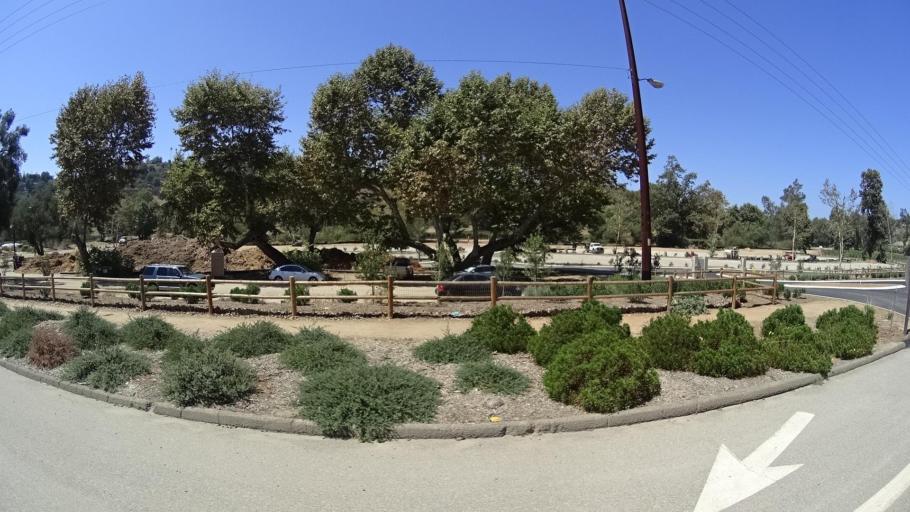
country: US
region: California
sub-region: San Diego County
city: Bonsall
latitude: 33.3427
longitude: -117.1905
